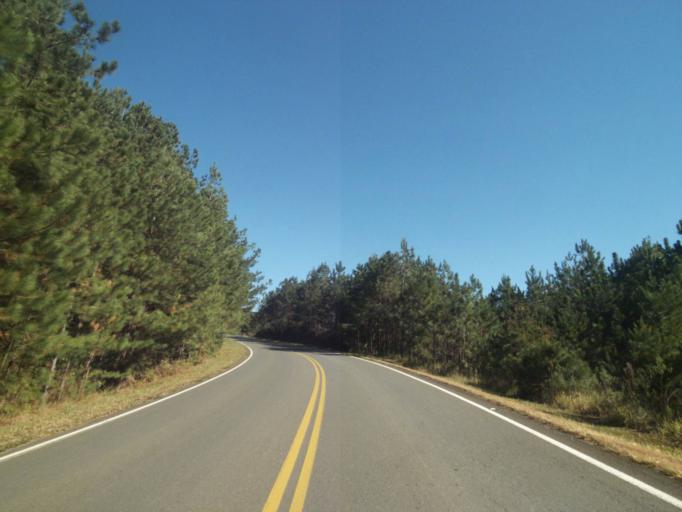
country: BR
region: Parana
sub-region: Telemaco Borba
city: Telemaco Borba
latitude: -24.4228
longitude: -50.5739
